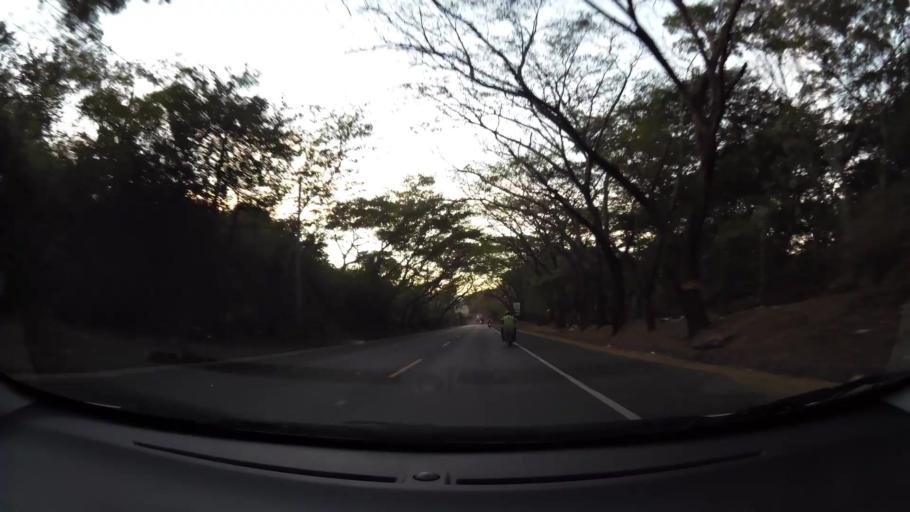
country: SV
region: San Miguel
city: Moncagua
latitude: 13.5029
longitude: -88.2215
